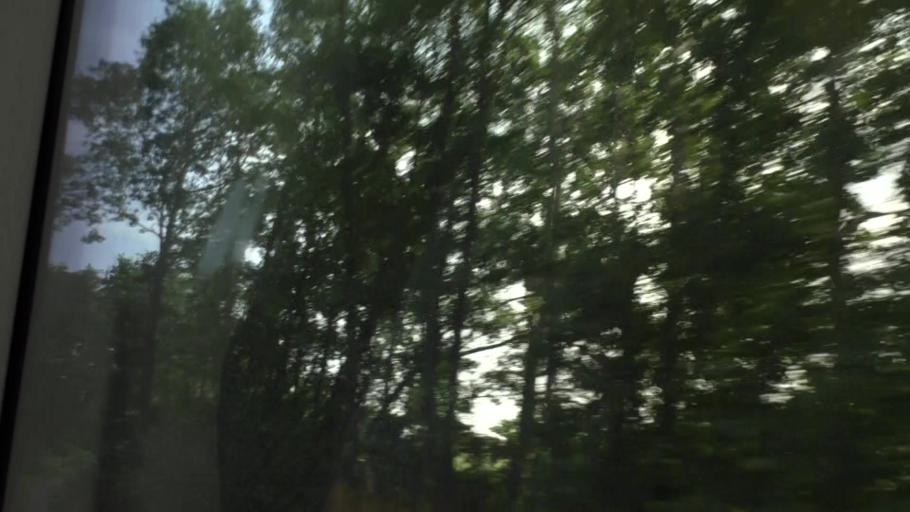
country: DE
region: Brandenburg
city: Beeskow
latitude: 52.1697
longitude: 14.3076
